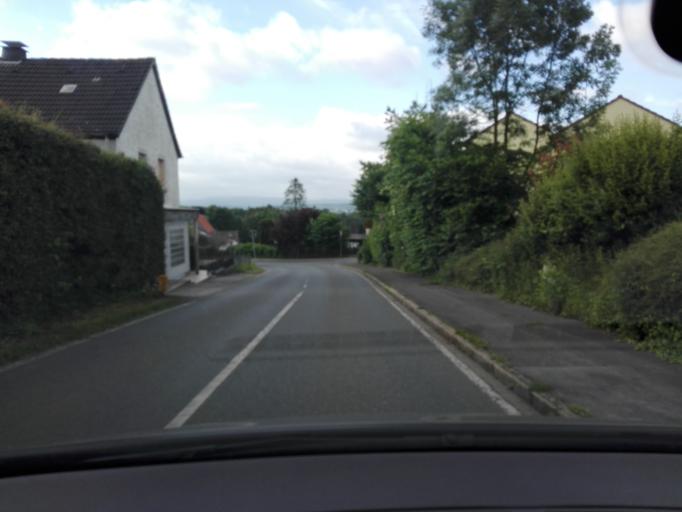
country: DE
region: North Rhine-Westphalia
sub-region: Regierungsbezirk Arnsberg
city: Frondenberg
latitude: 51.4780
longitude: 7.7677
